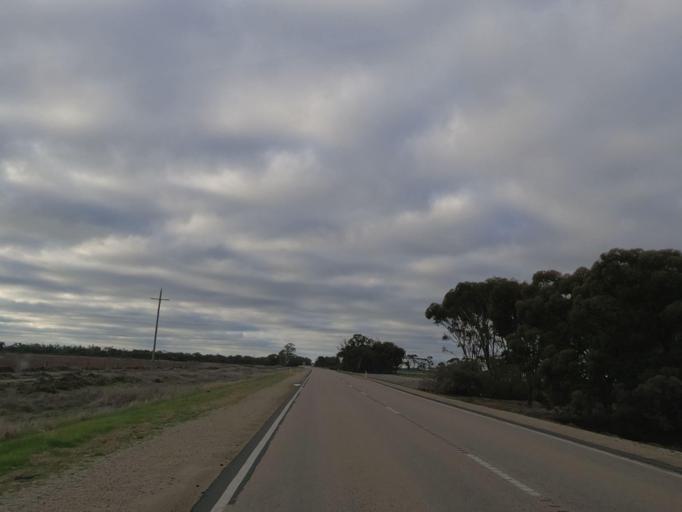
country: AU
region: Victoria
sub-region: Swan Hill
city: Swan Hill
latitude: -35.8256
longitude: 143.9472
